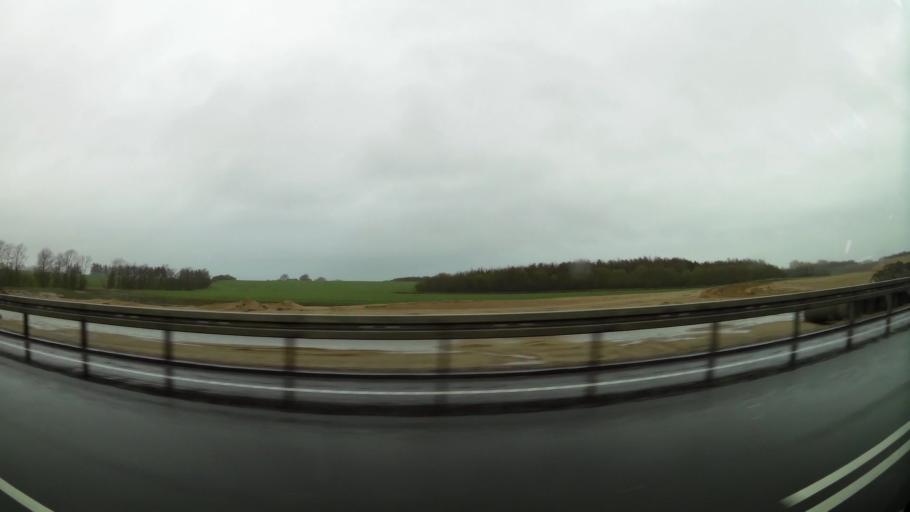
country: DK
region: Central Jutland
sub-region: Herning Kommune
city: Avlum
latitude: 56.2206
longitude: 8.8454
